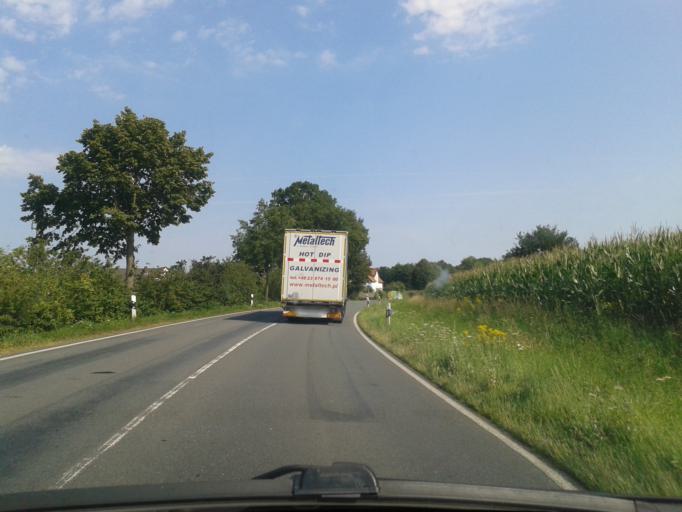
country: DE
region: North Rhine-Westphalia
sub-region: Regierungsbezirk Detmold
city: Verl
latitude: 51.8553
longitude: 8.5738
